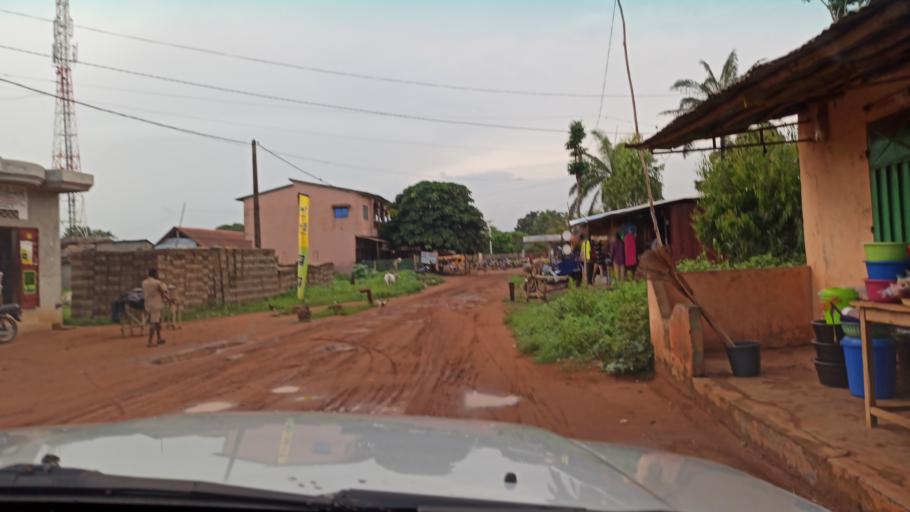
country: BJ
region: Queme
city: Porto-Novo
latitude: 6.4892
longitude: 2.6657
